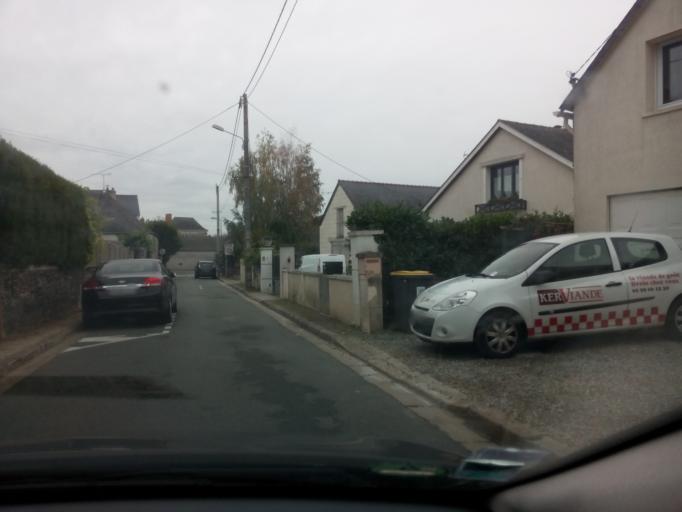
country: FR
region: Pays de la Loire
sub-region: Departement de Maine-et-Loire
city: Corne
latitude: 47.4707
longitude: -0.3514
